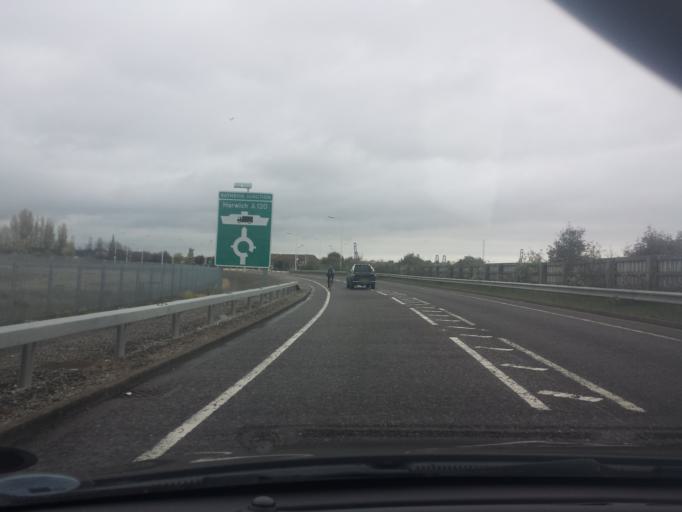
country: GB
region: England
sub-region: Essex
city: Dovercourt
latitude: 51.9392
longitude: 1.2797
